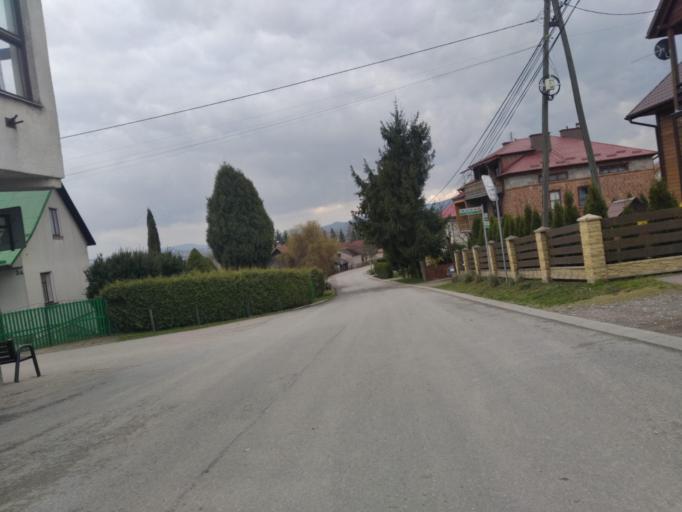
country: PL
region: Subcarpathian Voivodeship
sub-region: Powiat strzyzowski
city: Wisniowa
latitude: 49.8768
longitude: 21.6954
